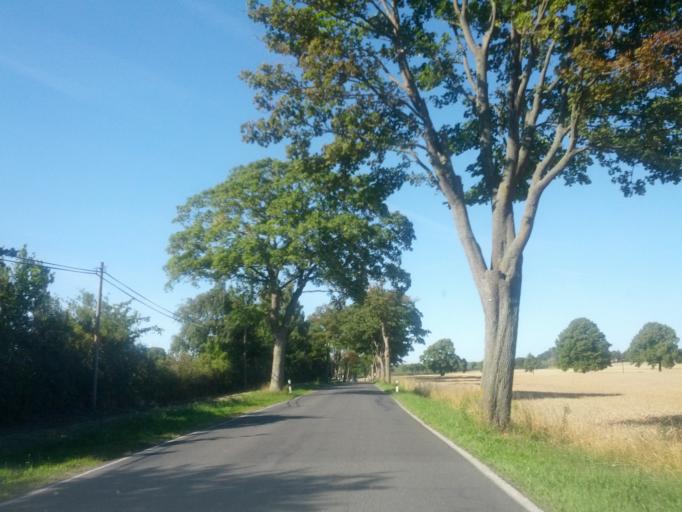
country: DE
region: Mecklenburg-Vorpommern
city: Bastorf
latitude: 54.1140
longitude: 11.6812
